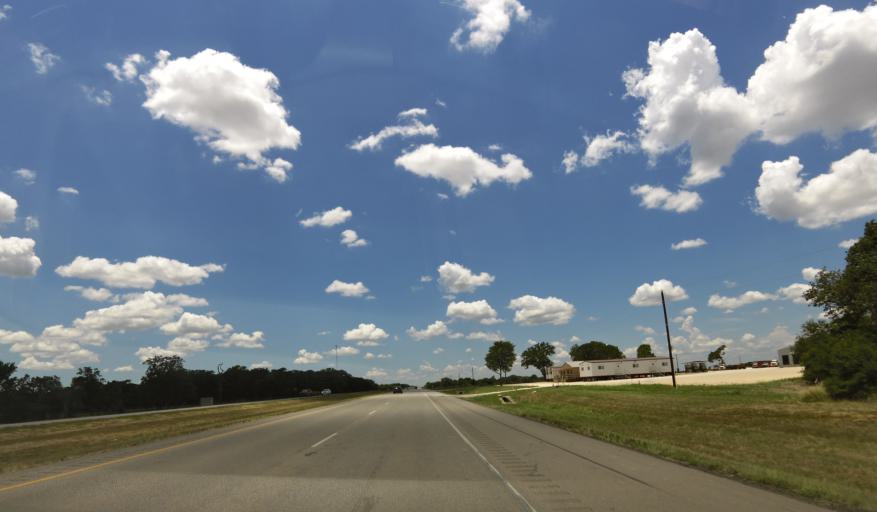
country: US
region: Texas
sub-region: Lee County
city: Giddings
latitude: 30.1485
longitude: -96.6971
